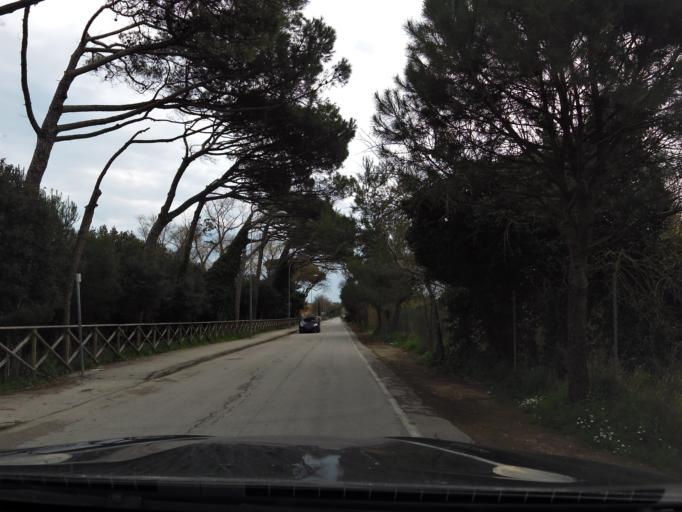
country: IT
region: The Marches
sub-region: Provincia di Macerata
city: Porto Recanati
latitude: 43.4194
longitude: 13.6710
